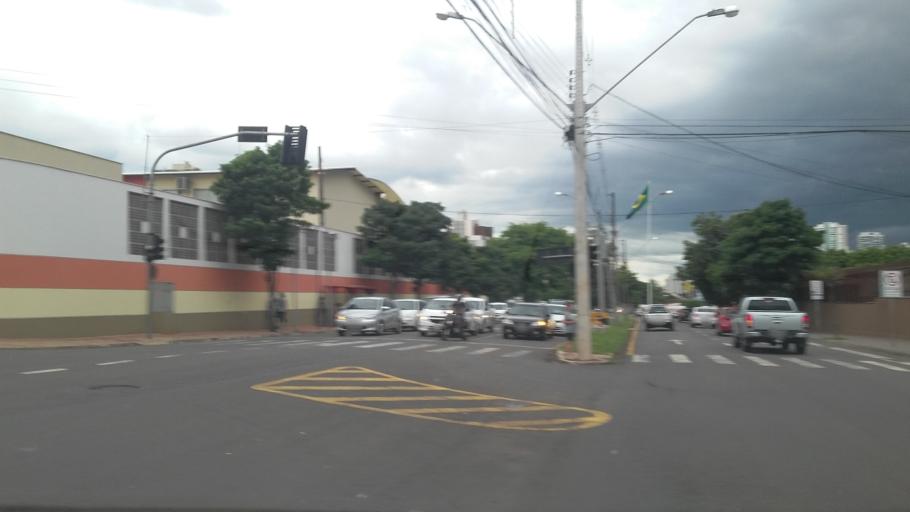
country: BR
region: Parana
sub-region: Londrina
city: Londrina
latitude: -23.3175
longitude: -51.1706
